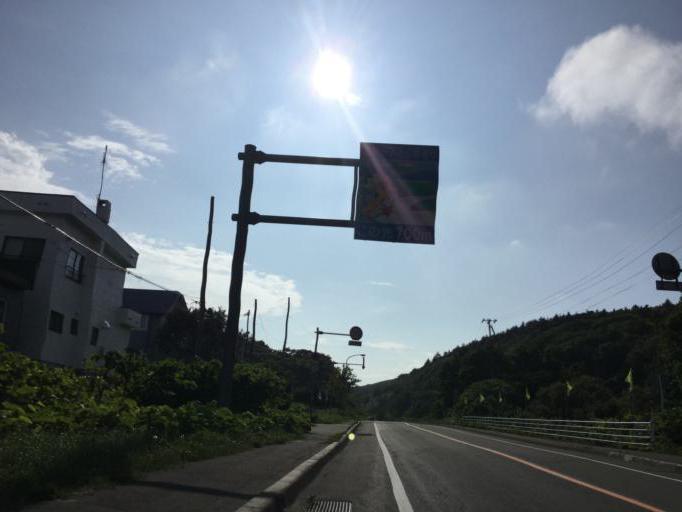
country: JP
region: Hokkaido
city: Wakkanai
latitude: 45.3827
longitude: 141.6647
